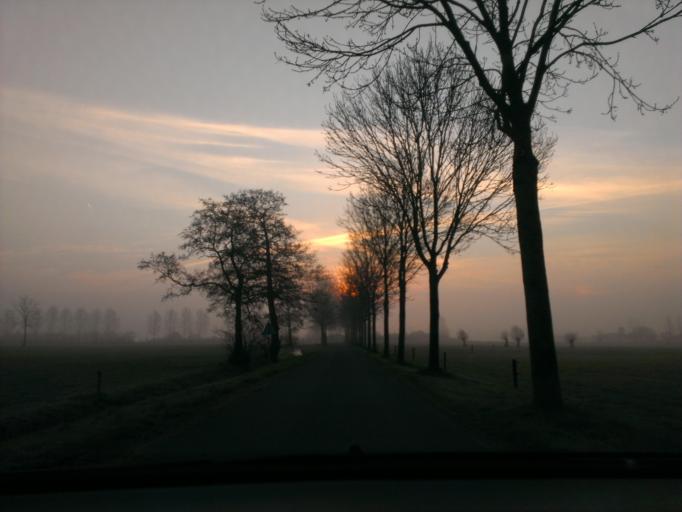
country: NL
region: Gelderland
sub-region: Gemeente Epe
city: Oene
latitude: 52.3332
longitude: 6.0476
